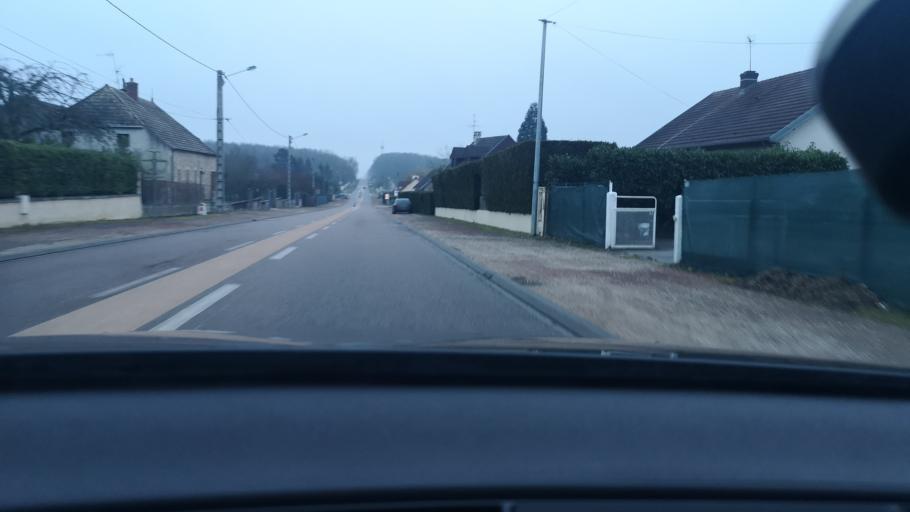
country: FR
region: Bourgogne
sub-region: Departement de la Cote-d'Or
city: Fenay
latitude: 47.1691
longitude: 5.0811
